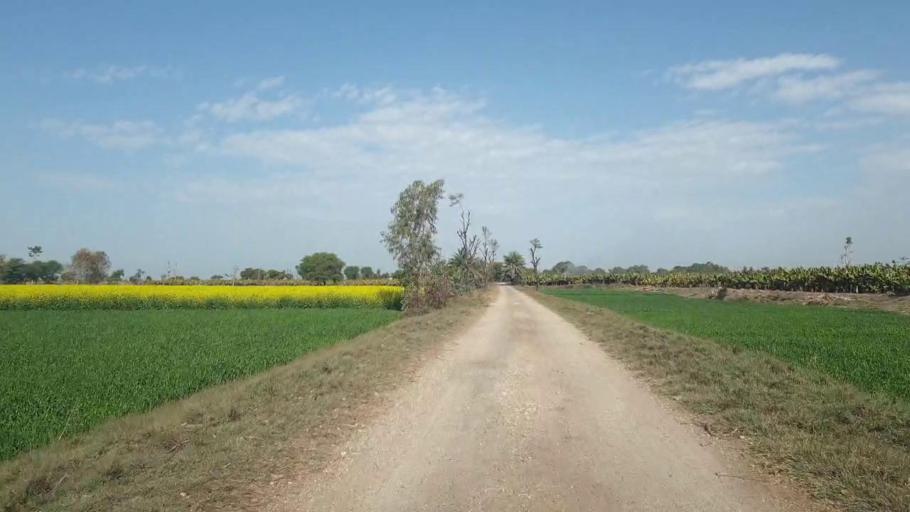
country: PK
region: Sindh
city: Hala
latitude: 25.9726
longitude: 68.3621
